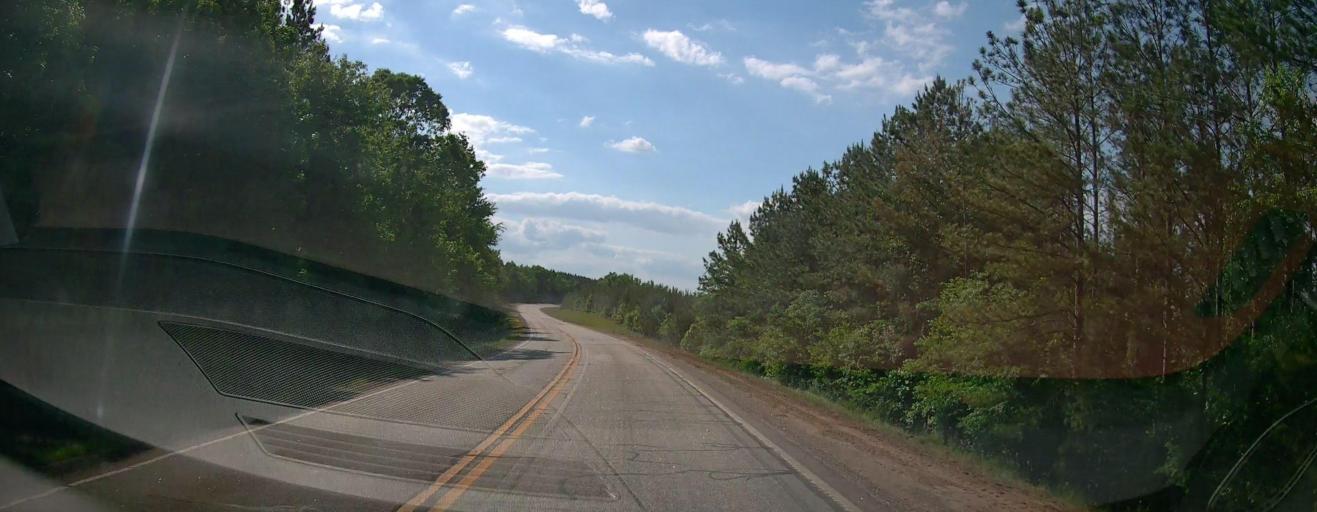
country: US
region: Georgia
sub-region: Washington County
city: Tennille
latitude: 32.9264
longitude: -83.0069
